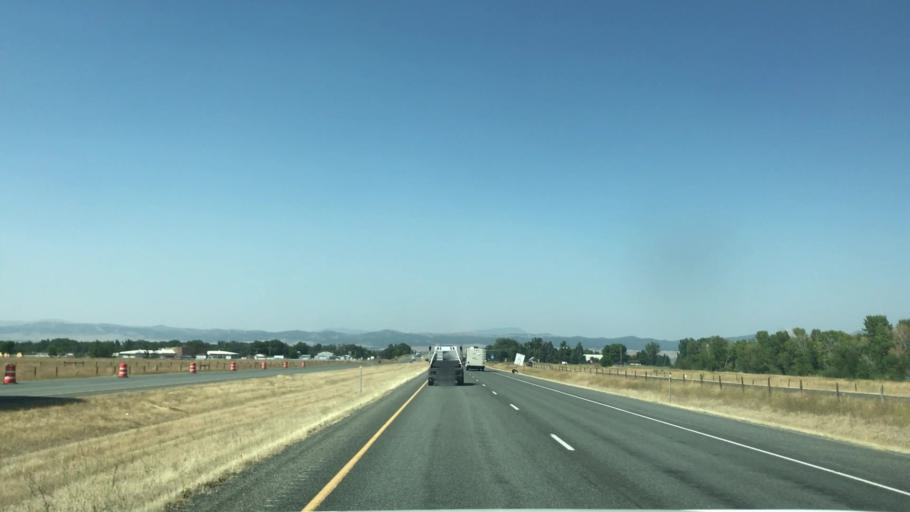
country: US
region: Montana
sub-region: Lewis and Clark County
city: Helena Valley West Central
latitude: 46.6539
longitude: -112.0113
